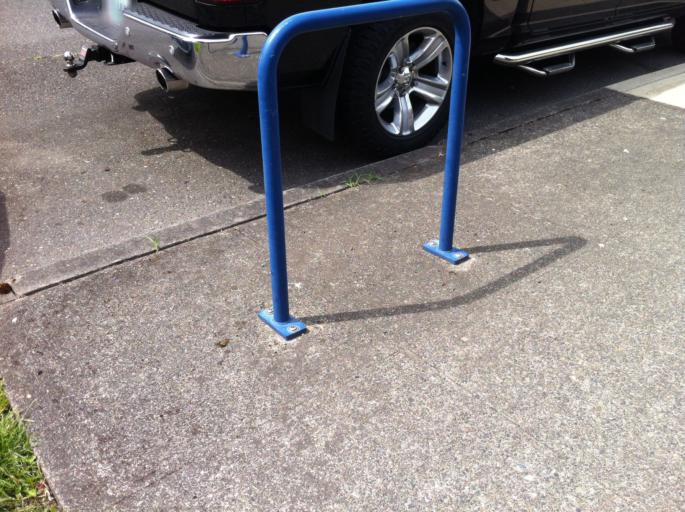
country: US
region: Oregon
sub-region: Multnomah County
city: Portland
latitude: 45.4816
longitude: -122.6757
